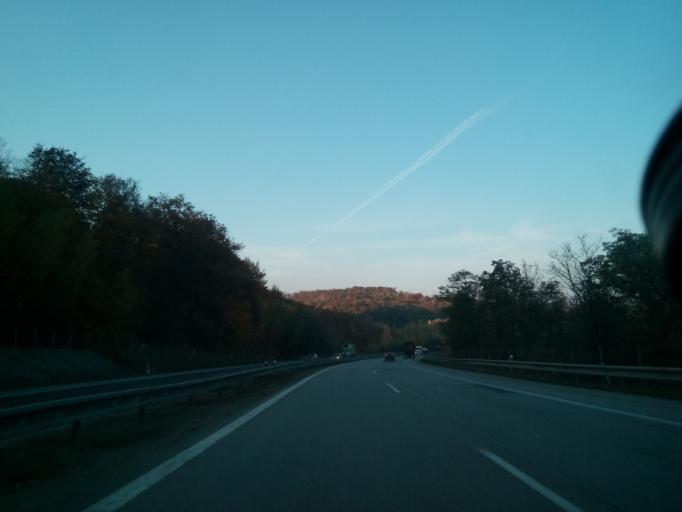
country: SK
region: Kosicky
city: Kosice
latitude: 48.7773
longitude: 21.2926
